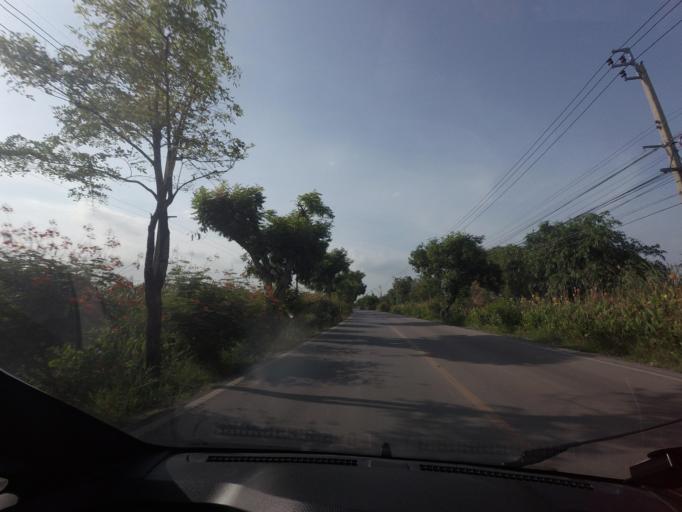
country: TH
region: Samut Prakan
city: Ban Khlong Bang Sao Thong
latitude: 13.7032
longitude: 100.8539
